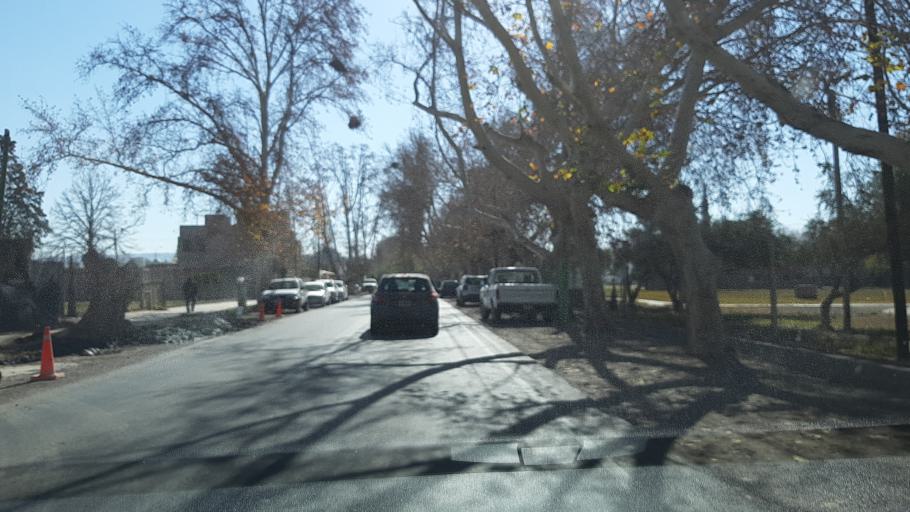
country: AR
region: San Juan
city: San Juan
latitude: -31.5296
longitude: -68.5947
